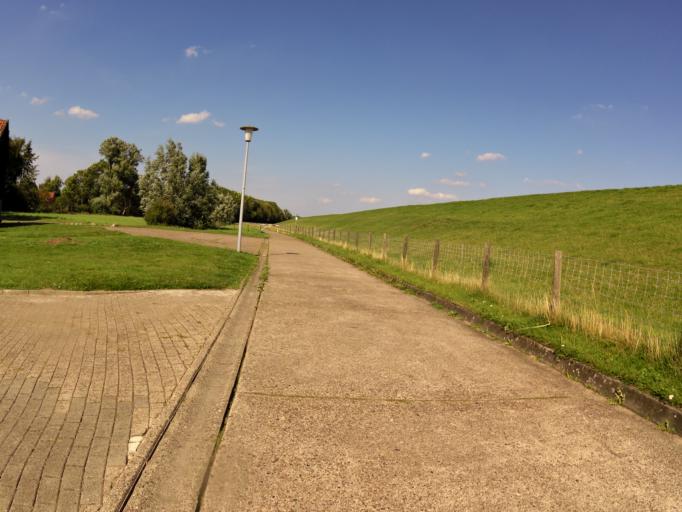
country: DE
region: Lower Saxony
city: Brake (Unterweser)
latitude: 53.3995
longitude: 8.4629
